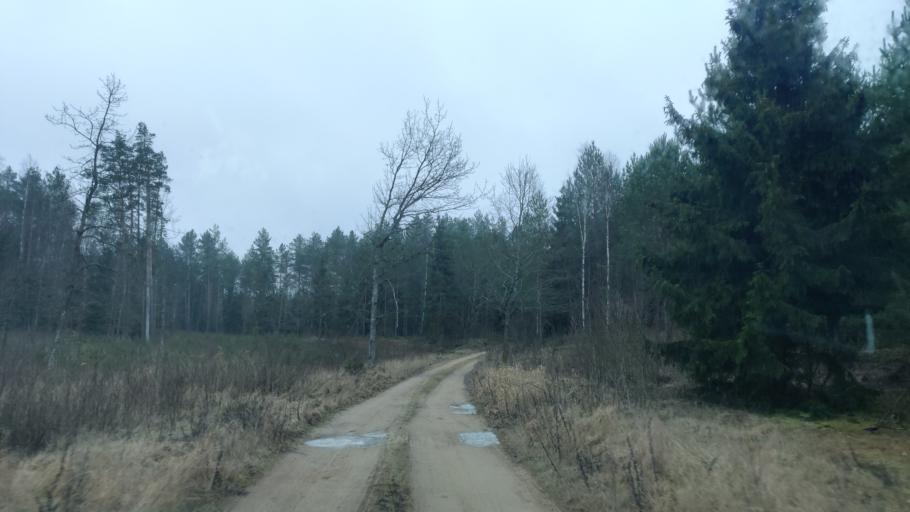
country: LT
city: Trakai
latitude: 54.5597
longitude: 24.9579
